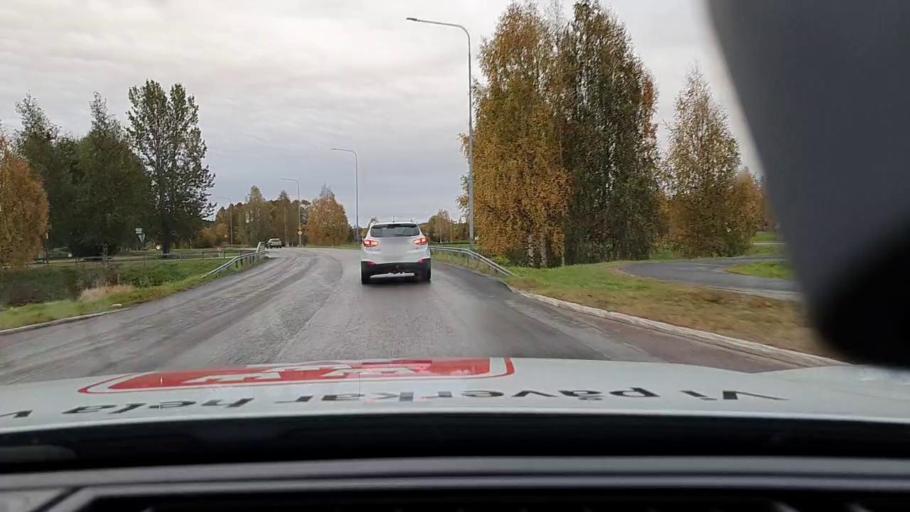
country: SE
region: Norrbotten
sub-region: Bodens Kommun
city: Saevast
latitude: 65.7578
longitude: 21.7442
